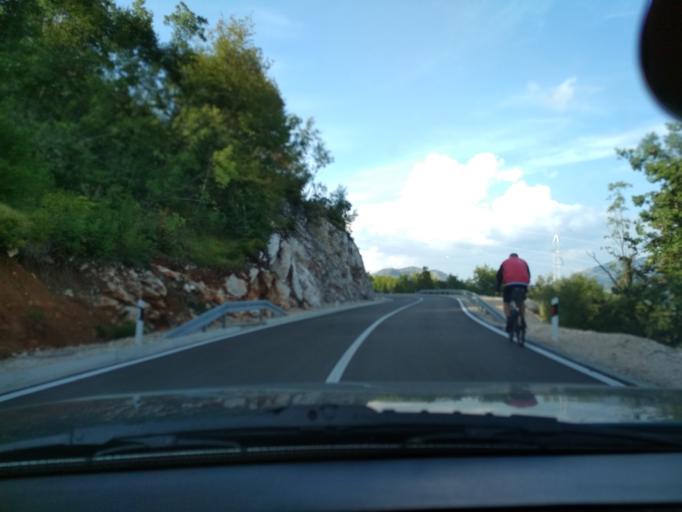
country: ME
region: Cetinje
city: Cetinje
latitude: 42.4210
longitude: 18.8743
